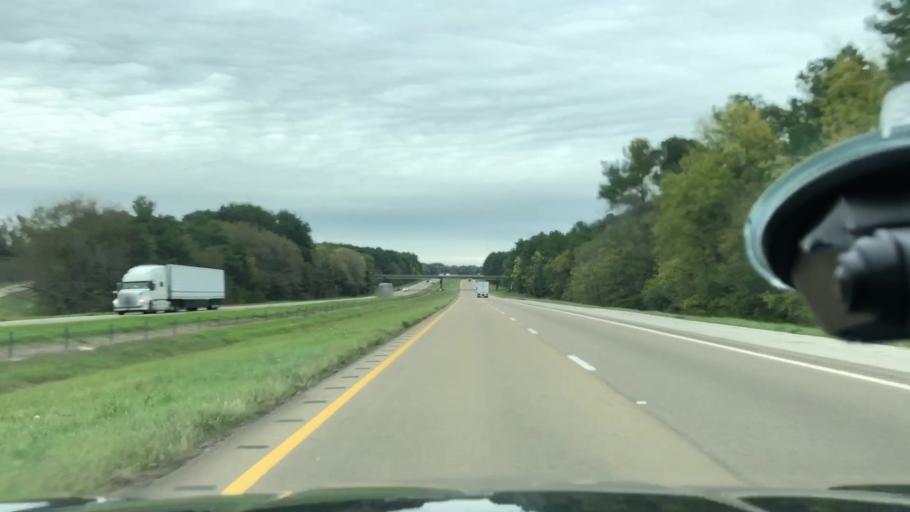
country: US
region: Texas
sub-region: Titus County
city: Mount Pleasant
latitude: 33.2204
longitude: -94.8931
